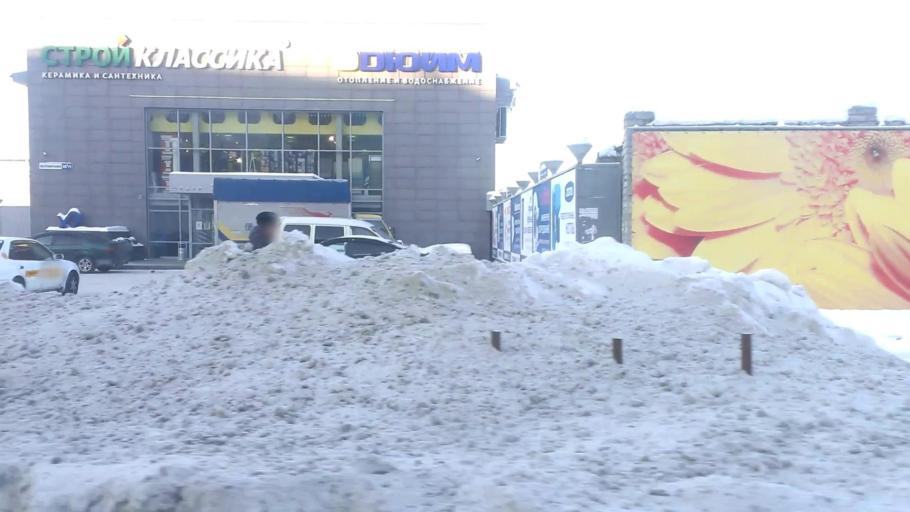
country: RU
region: Altai Krai
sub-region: Gorod Barnaulskiy
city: Barnaul
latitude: 53.3431
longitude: 83.7508
